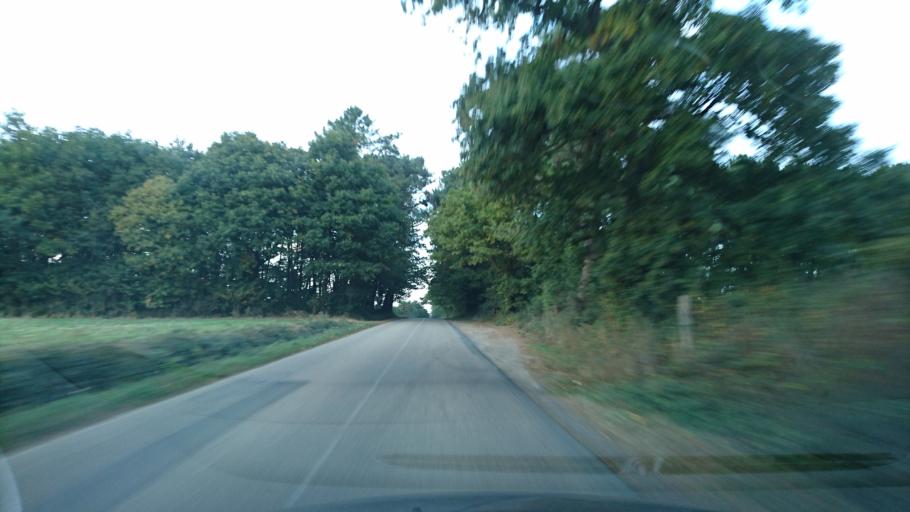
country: FR
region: Brittany
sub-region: Departement d'Ille-et-Vilaine
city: Saint-Just
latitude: 47.7963
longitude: -2.0092
